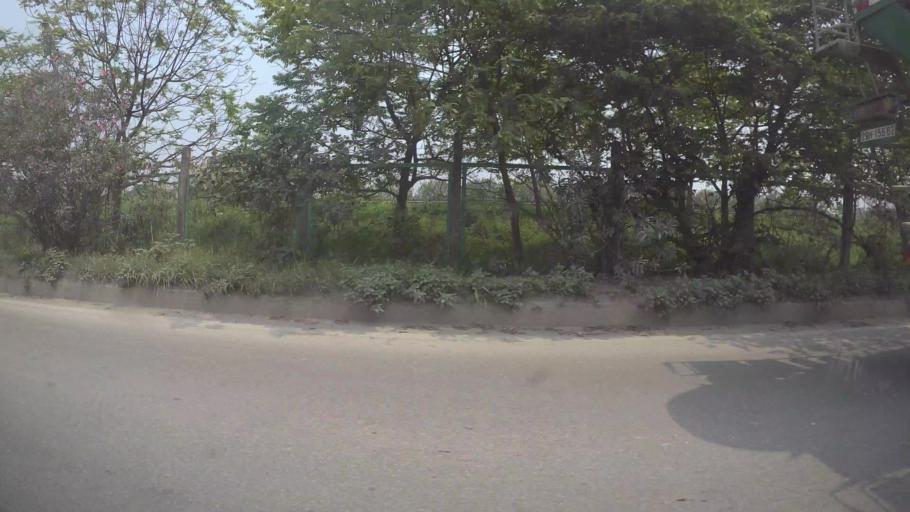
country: VN
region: Ha Noi
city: Cau Dien
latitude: 21.0102
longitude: 105.7285
